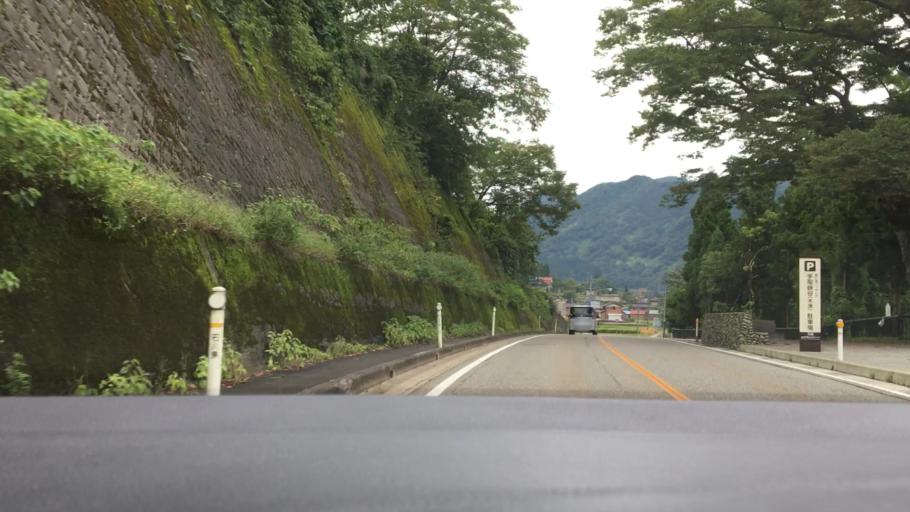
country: JP
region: Ishikawa
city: Tsurugi-asahimachi
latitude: 36.3142
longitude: 136.6481
